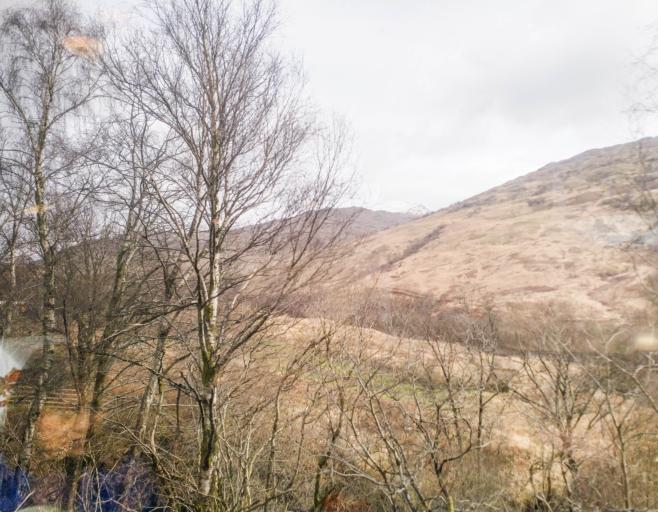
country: GB
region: Scotland
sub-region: Argyll and Bute
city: Garelochhead
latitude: 56.3511
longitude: -4.7016
